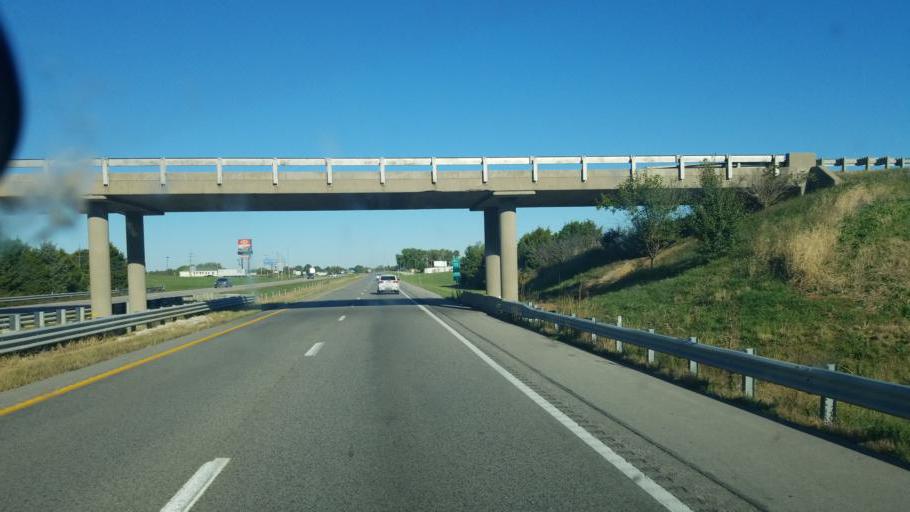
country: US
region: Missouri
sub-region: Warren County
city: Warrenton
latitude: 38.8387
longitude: -91.2241
